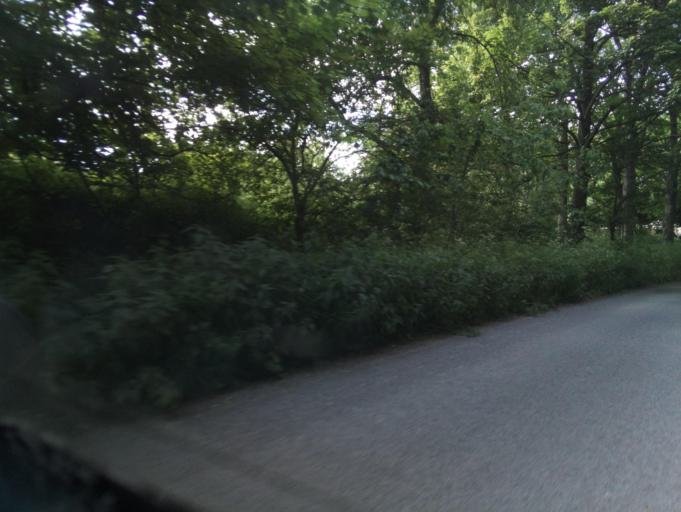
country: GB
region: England
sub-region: Wiltshire
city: Rushall
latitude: 51.2709
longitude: -1.8041
